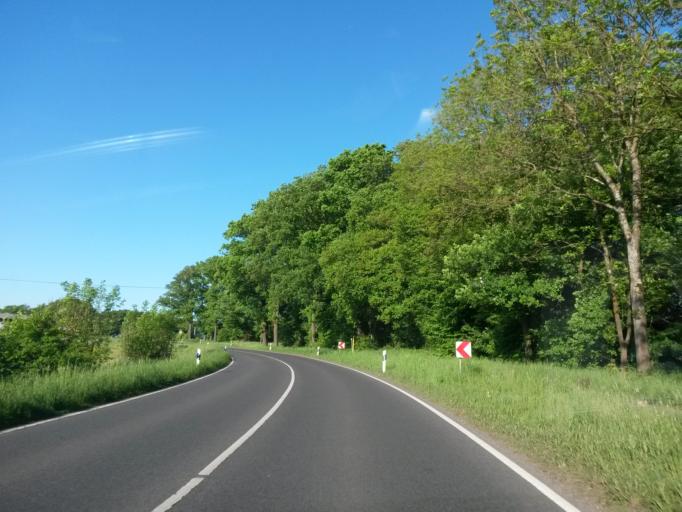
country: DE
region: North Rhine-Westphalia
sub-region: Regierungsbezirk Koln
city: Overath
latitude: 50.8606
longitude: 7.3090
